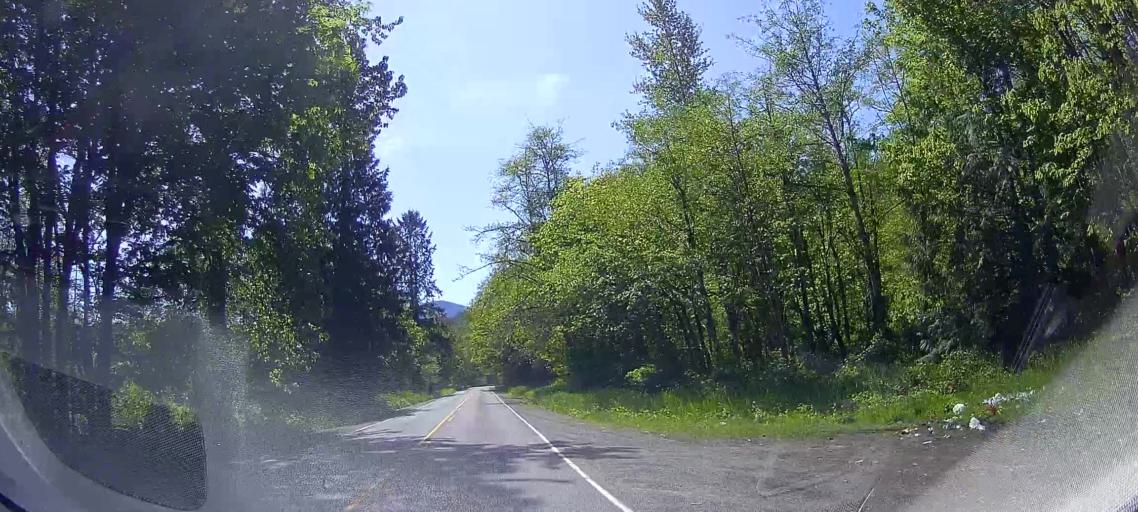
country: US
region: Washington
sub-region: Snohomish County
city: Darrington
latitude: 48.5118
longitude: -121.7245
